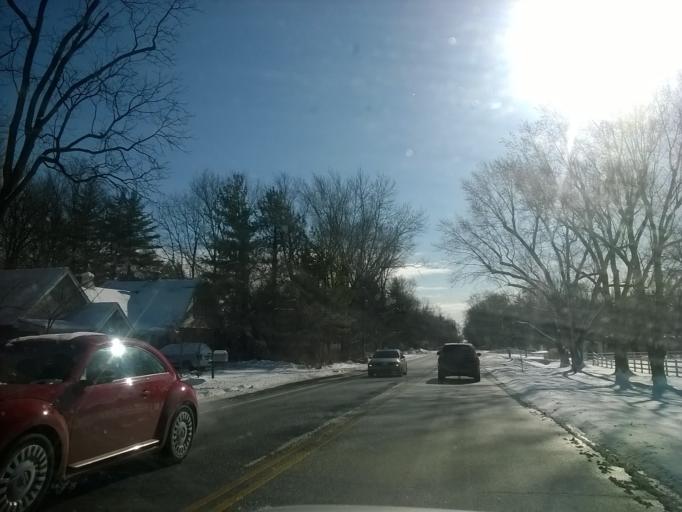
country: US
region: Indiana
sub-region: Hamilton County
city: Carmel
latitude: 39.9534
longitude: -86.1268
